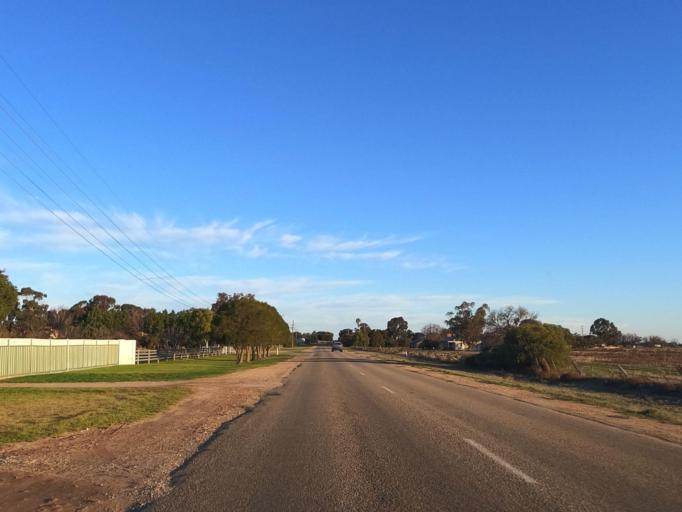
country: AU
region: Victoria
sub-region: Swan Hill
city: Swan Hill
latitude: -35.3572
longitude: 143.5523
